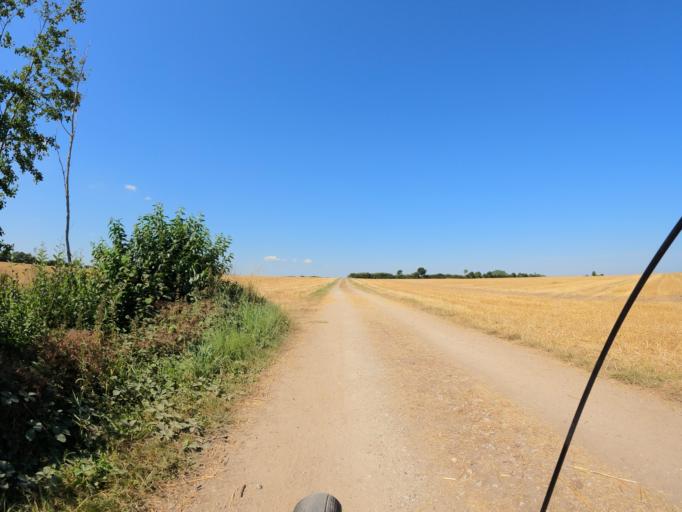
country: DE
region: Schleswig-Holstein
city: Steinbergkirche
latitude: 54.7848
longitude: 9.7572
